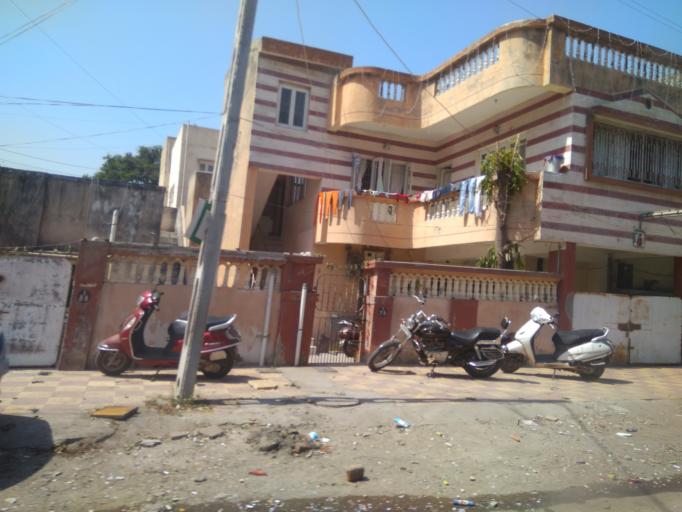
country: IN
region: Gujarat
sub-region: Jamnagar
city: Jamnagar
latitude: 22.4841
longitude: 70.0551
